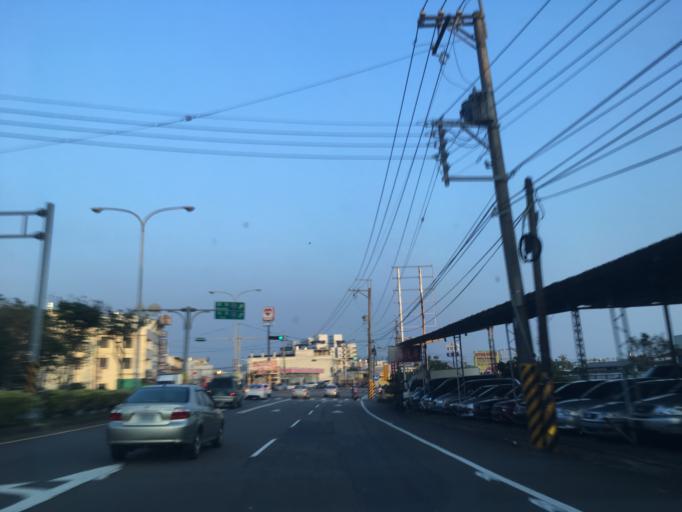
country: TW
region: Taiwan
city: Zhongxing New Village
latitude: 23.9959
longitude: 120.6645
